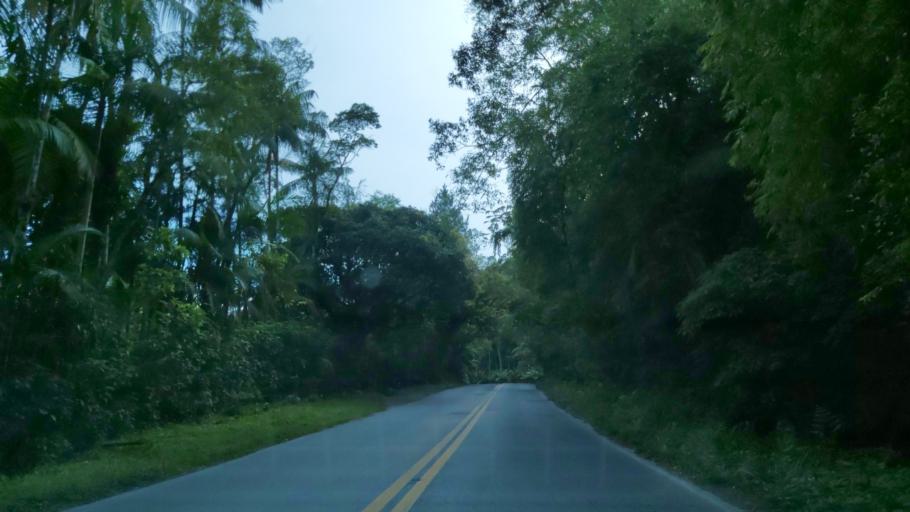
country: BR
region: Sao Paulo
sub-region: Miracatu
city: Miracatu
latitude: -24.0660
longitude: -47.5962
